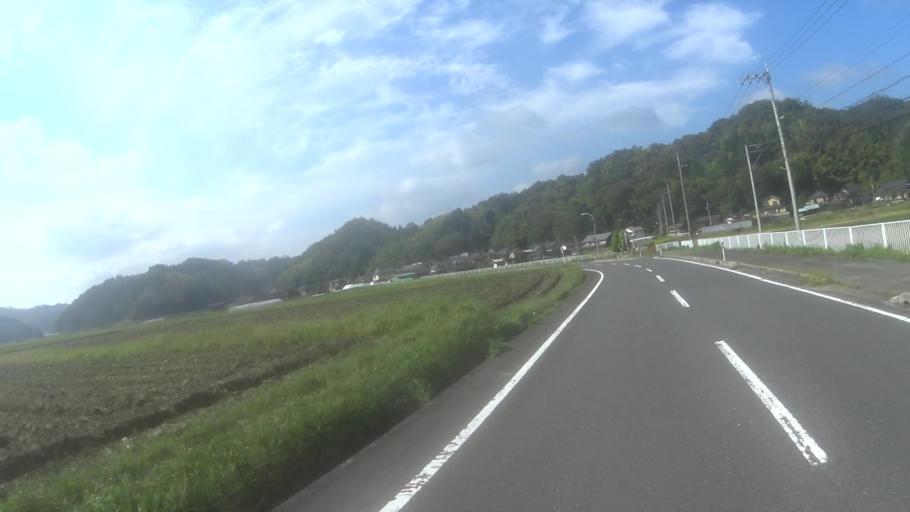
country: JP
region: Kyoto
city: Miyazu
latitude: 35.5963
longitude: 135.1364
